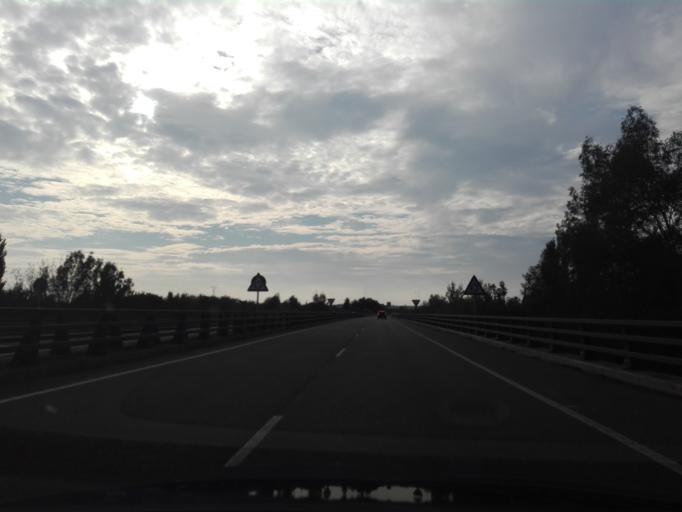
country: ES
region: Extremadura
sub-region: Provincia de Badajoz
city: Badajoz
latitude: 38.9178
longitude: -6.9569
